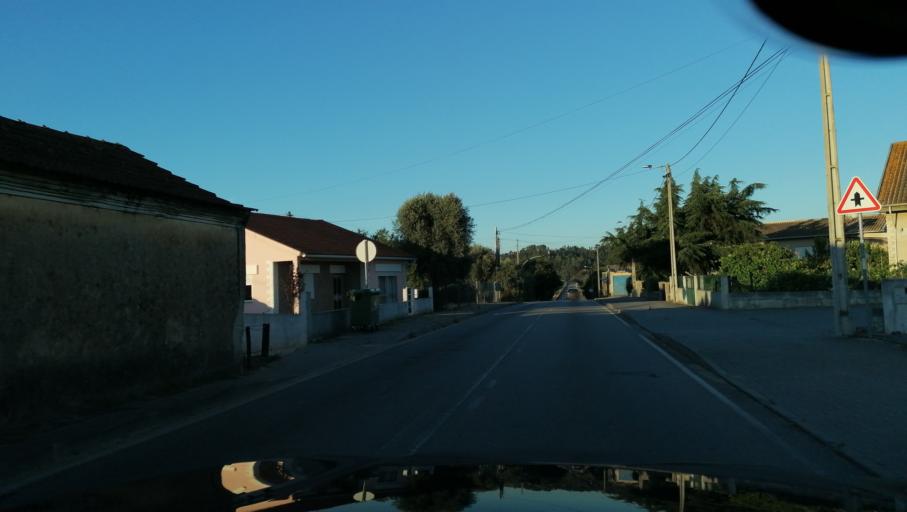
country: PT
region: Aveiro
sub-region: Oliveira do Bairro
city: Oia
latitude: 40.5488
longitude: -8.5036
